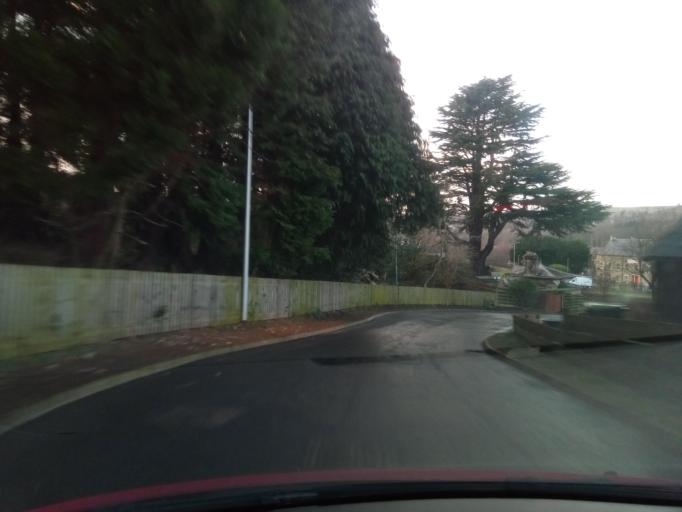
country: GB
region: Scotland
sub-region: The Scottish Borders
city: Hawick
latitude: 55.4291
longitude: -2.7675
